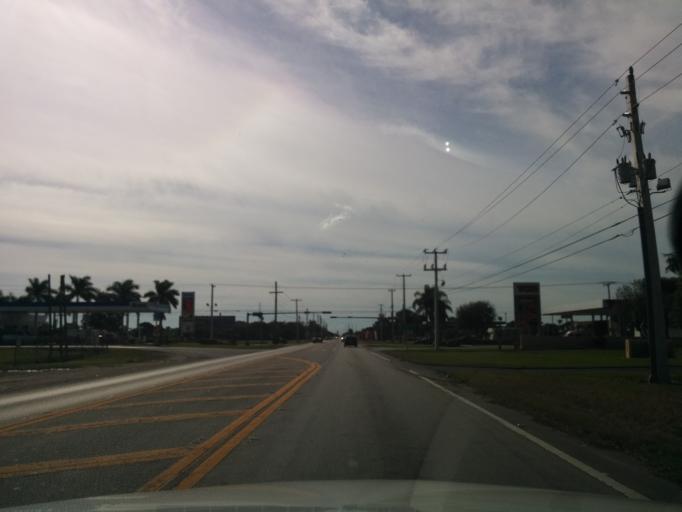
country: US
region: Florida
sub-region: Miami-Dade County
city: Naranja
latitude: 25.5369
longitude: -80.4780
